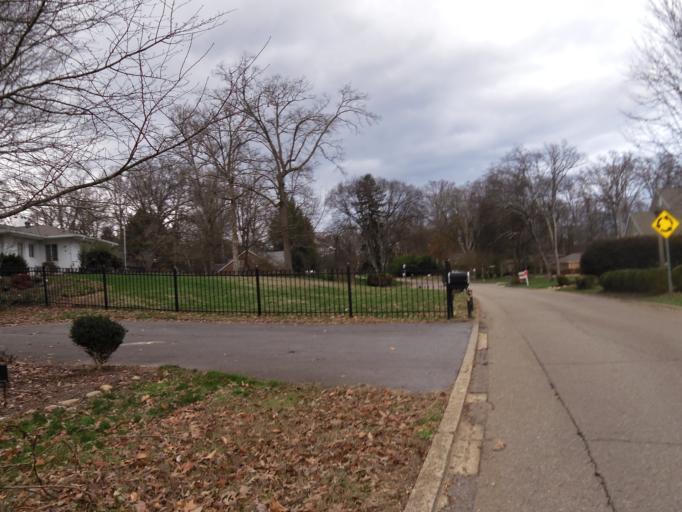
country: US
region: Tennessee
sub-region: Knox County
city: Knoxville
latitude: 35.9356
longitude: -83.9611
